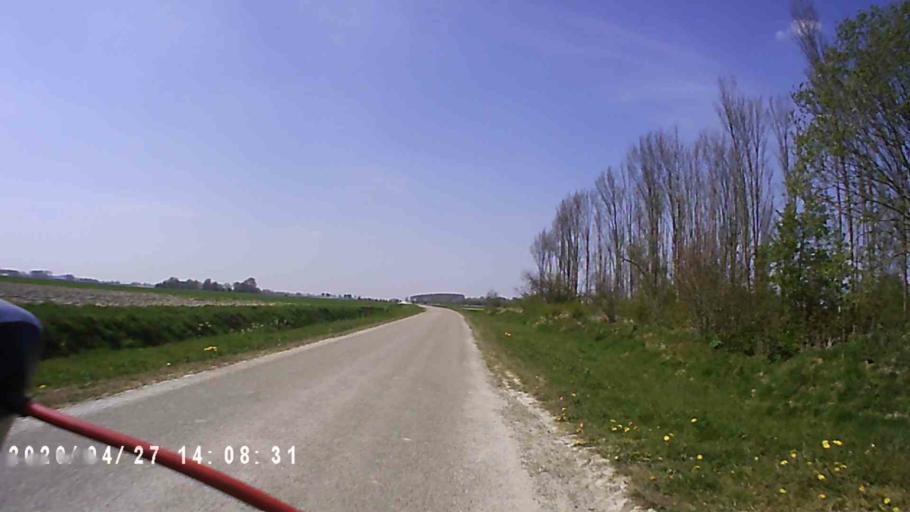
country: NL
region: Groningen
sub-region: Gemeente Zuidhorn
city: Oldehove
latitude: 53.3460
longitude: 6.3924
